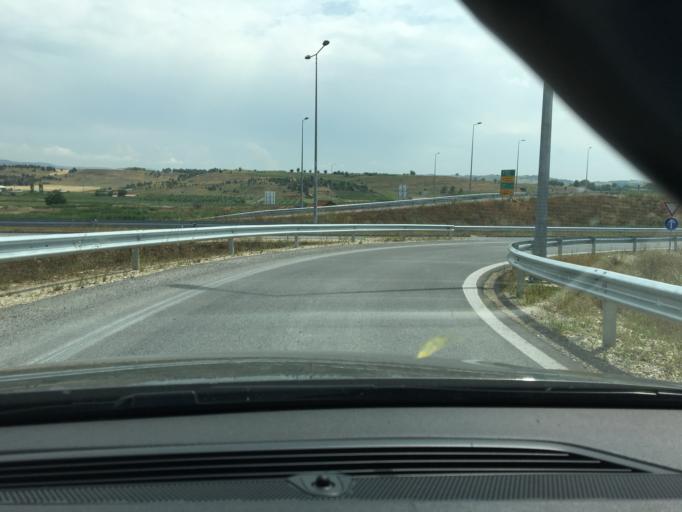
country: MK
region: Sveti Nikole
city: Sveti Nikole
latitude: 41.8779
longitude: 21.9369
